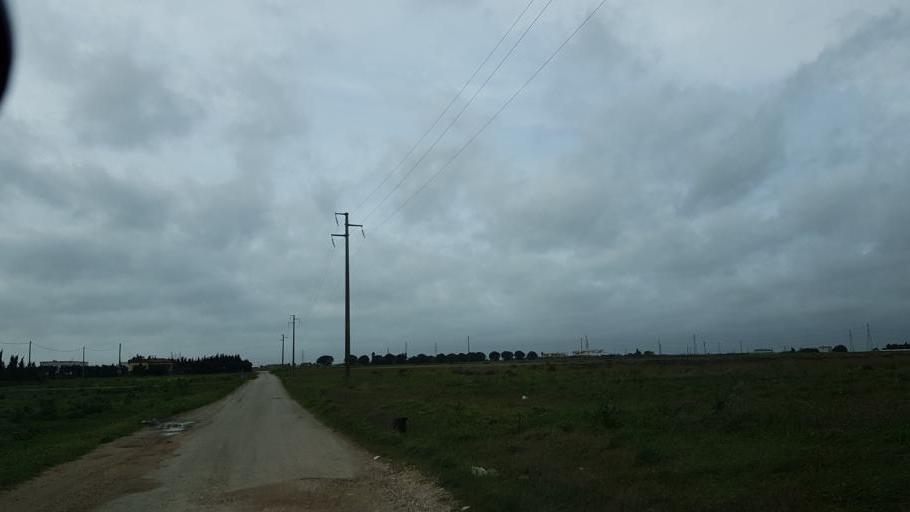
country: IT
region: Apulia
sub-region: Provincia di Brindisi
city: La Rosa
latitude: 40.5980
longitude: 17.9200
